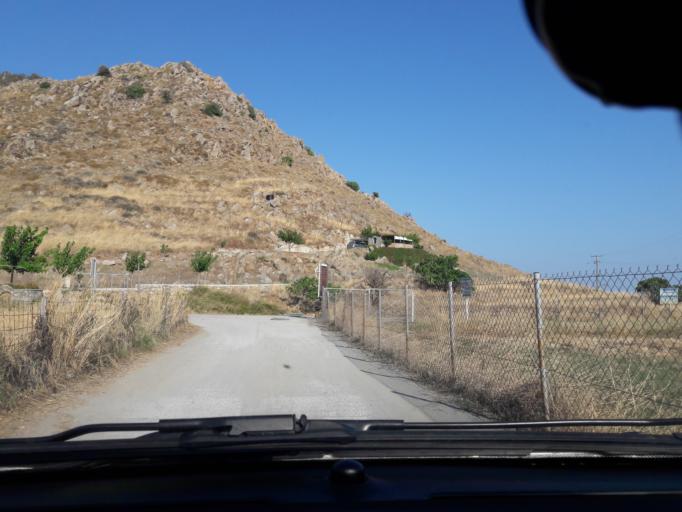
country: GR
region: North Aegean
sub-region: Nomos Lesvou
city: Myrina
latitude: 39.8440
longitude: 25.0835
